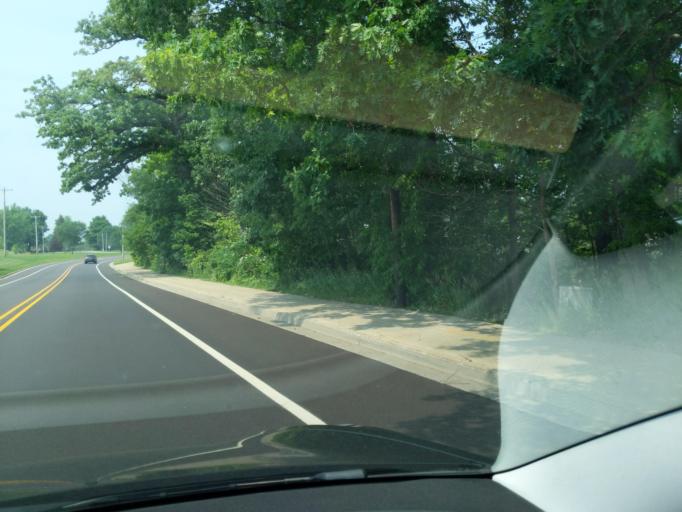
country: US
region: Michigan
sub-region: Clinton County
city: DeWitt
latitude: 42.8319
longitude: -84.5724
